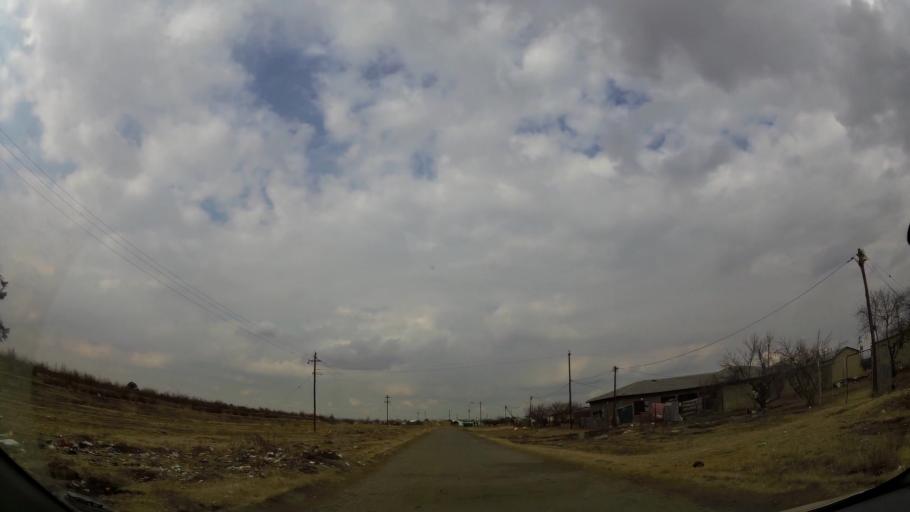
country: ZA
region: Orange Free State
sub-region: Fezile Dabi District Municipality
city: Sasolburg
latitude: -26.8792
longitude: 27.8794
